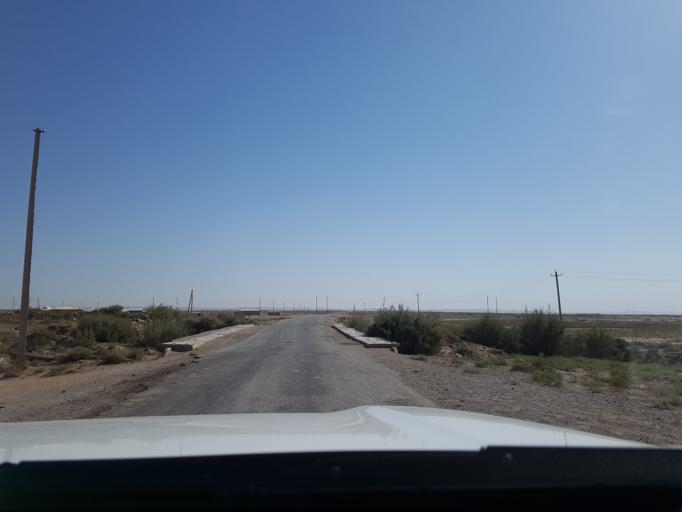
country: IR
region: Razavi Khorasan
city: Sarakhs
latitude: 36.5142
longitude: 61.2529
